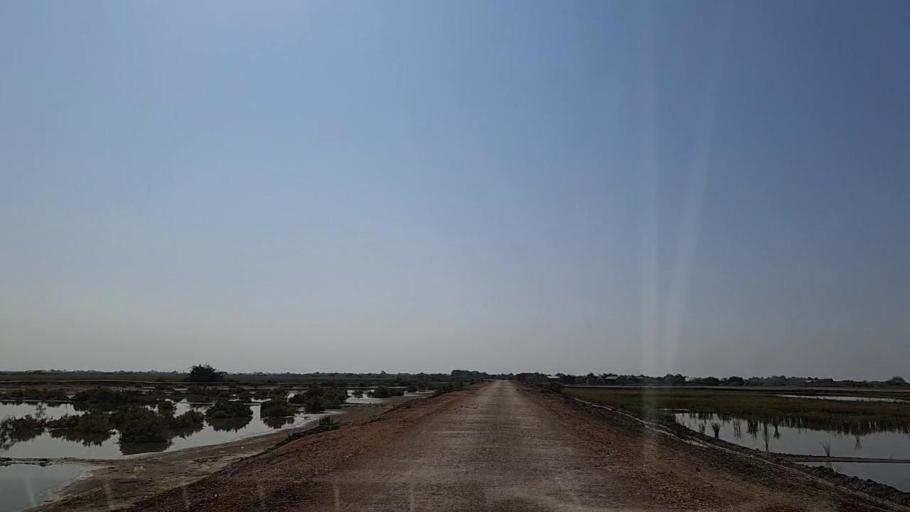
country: PK
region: Sindh
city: Chuhar Jamali
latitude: 24.4765
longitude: 68.0913
